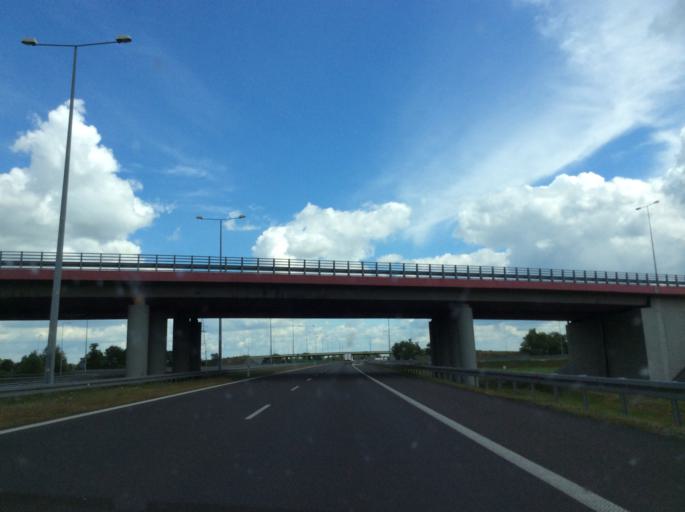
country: PL
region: Greater Poland Voivodeship
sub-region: Powiat turecki
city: Brudzew
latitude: 52.1407
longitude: 18.6066
